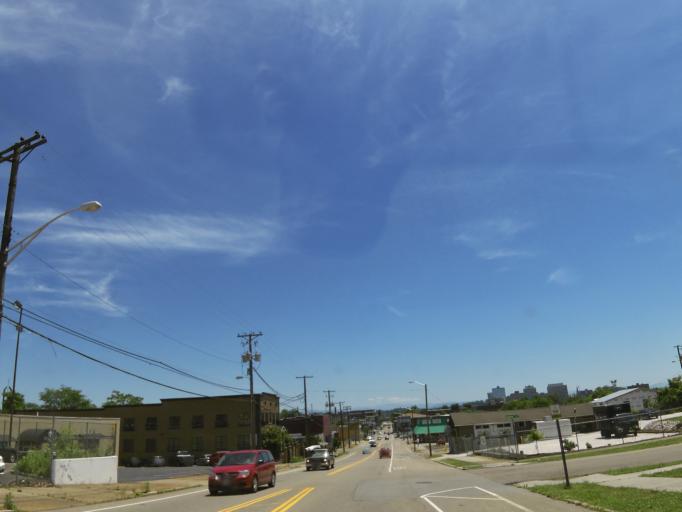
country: US
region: Tennessee
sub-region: Knox County
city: Knoxville
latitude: 35.9792
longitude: -83.9271
